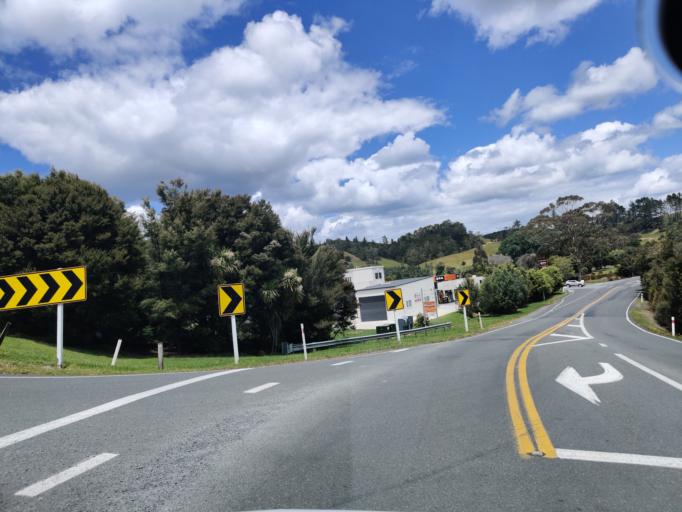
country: NZ
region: Northland
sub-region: Far North District
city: Paihia
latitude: -35.2872
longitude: 174.1492
